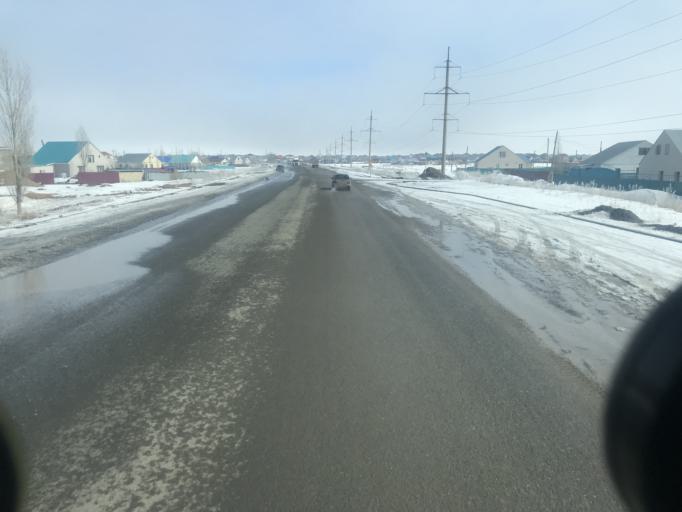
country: KZ
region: Aqtoebe
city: Aqtobe
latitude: 50.2767
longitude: 57.2726
